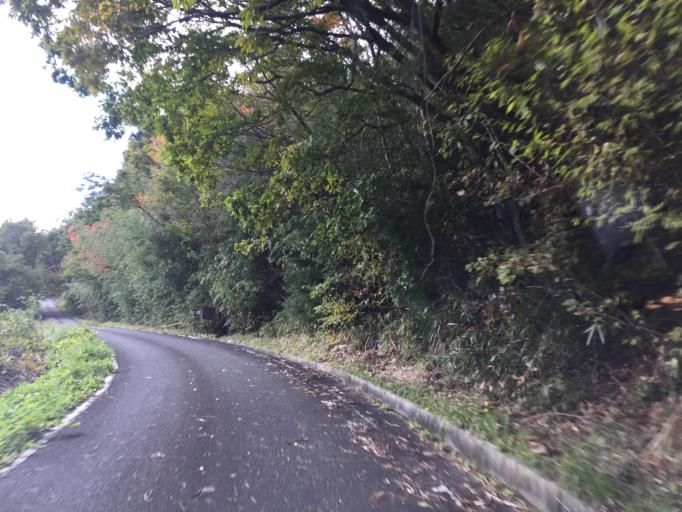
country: JP
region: Fukushima
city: Nihommatsu
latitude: 37.6757
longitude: 140.3941
